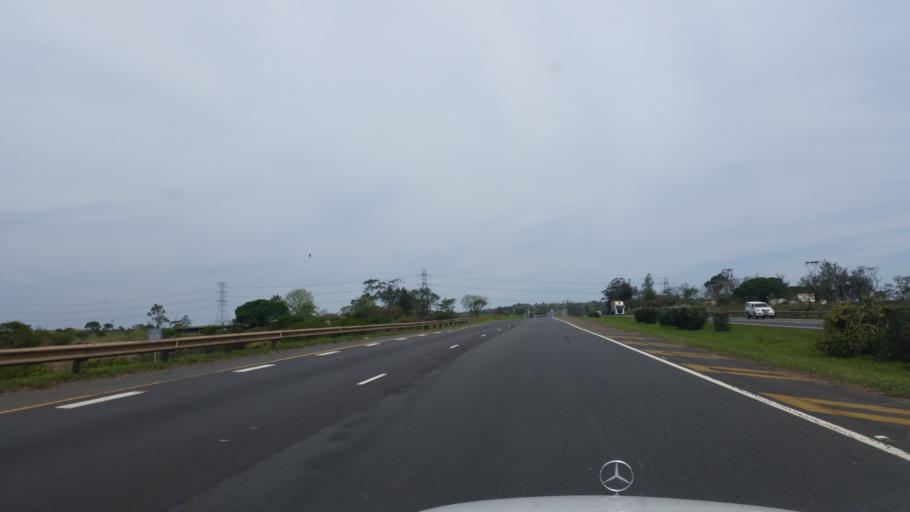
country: ZA
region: KwaZulu-Natal
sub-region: uMgungundlovu District Municipality
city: Camperdown
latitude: -29.6953
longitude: 30.4855
